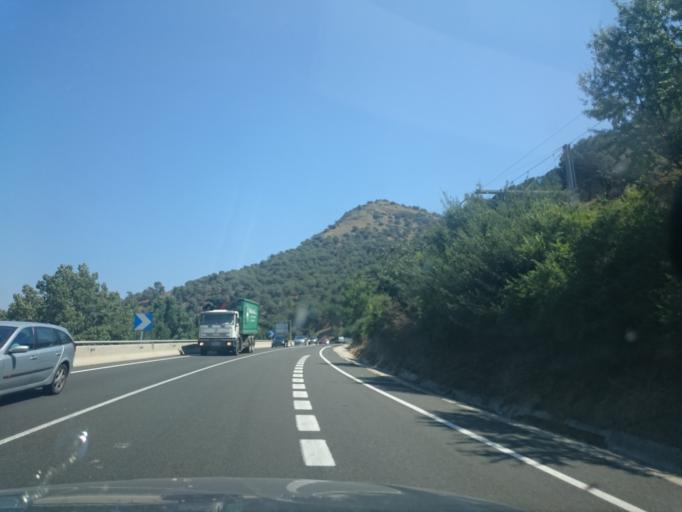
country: ES
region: Catalonia
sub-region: Provincia de Barcelona
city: Capellades
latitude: 41.5234
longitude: 1.6928
